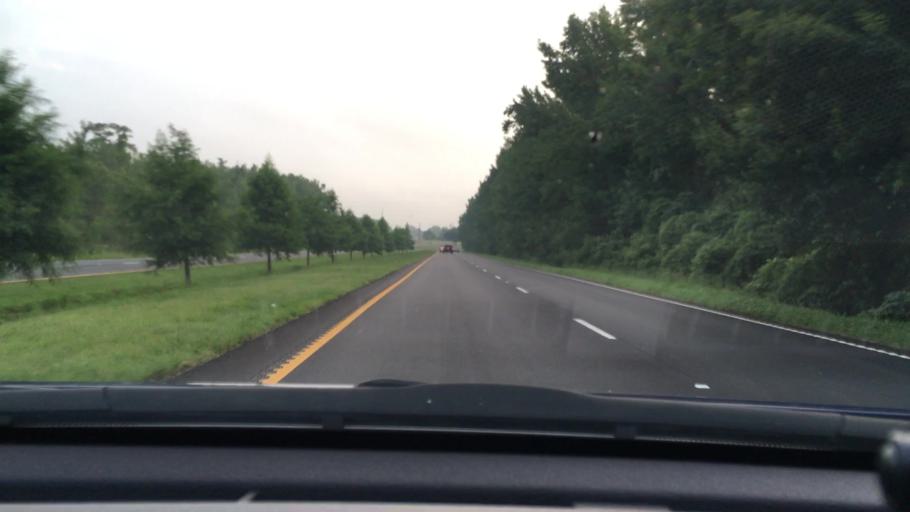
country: US
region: South Carolina
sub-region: Sumter County
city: South Sumter
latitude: 33.8769
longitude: -80.3519
